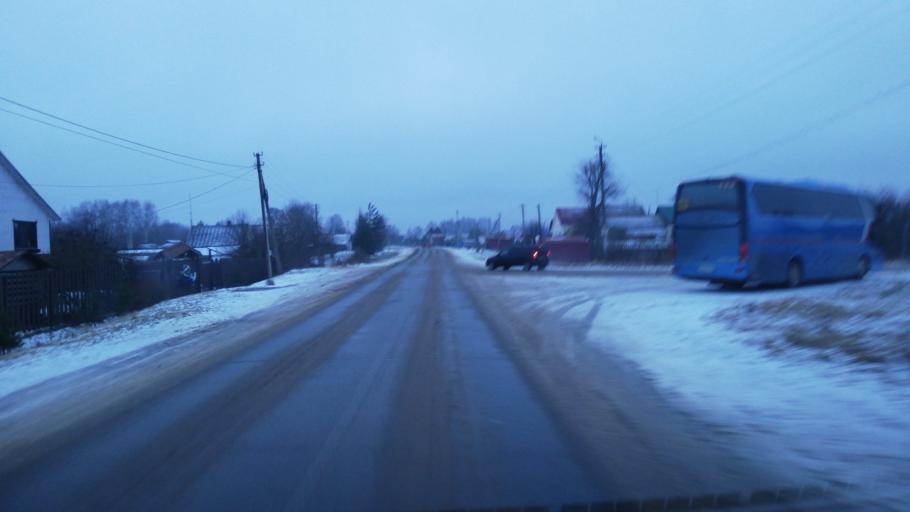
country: RU
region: Kostroma
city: Oktyabr'skiy
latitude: 57.7118
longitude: 41.1587
